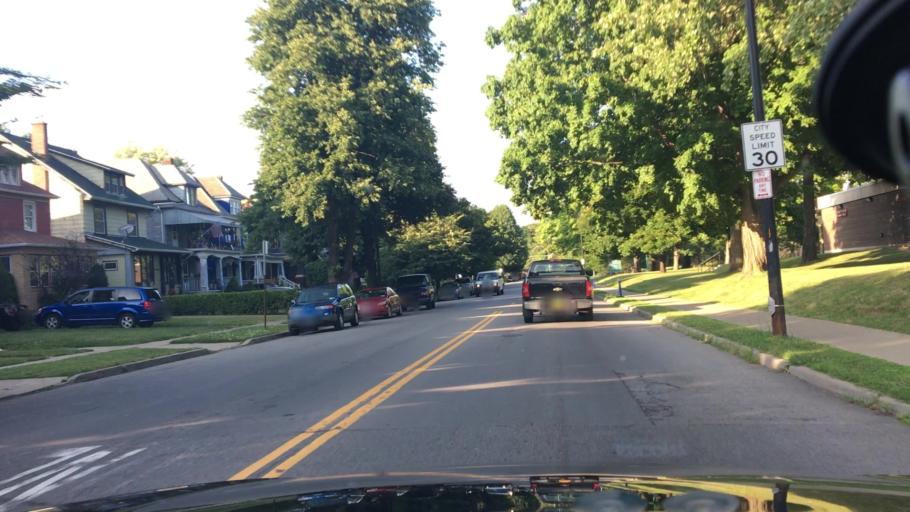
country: US
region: New York
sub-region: Erie County
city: West Seneca
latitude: 42.8486
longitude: -78.8122
